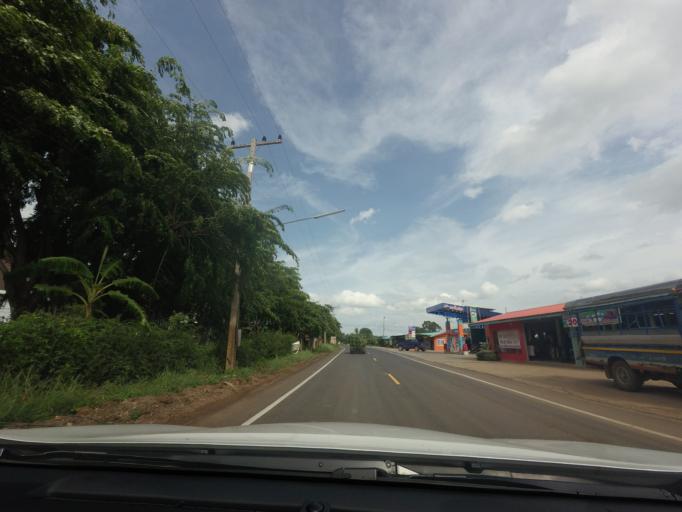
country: TH
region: Nakhon Ratchasima
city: Pak Chong
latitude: 14.5476
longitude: 101.4399
